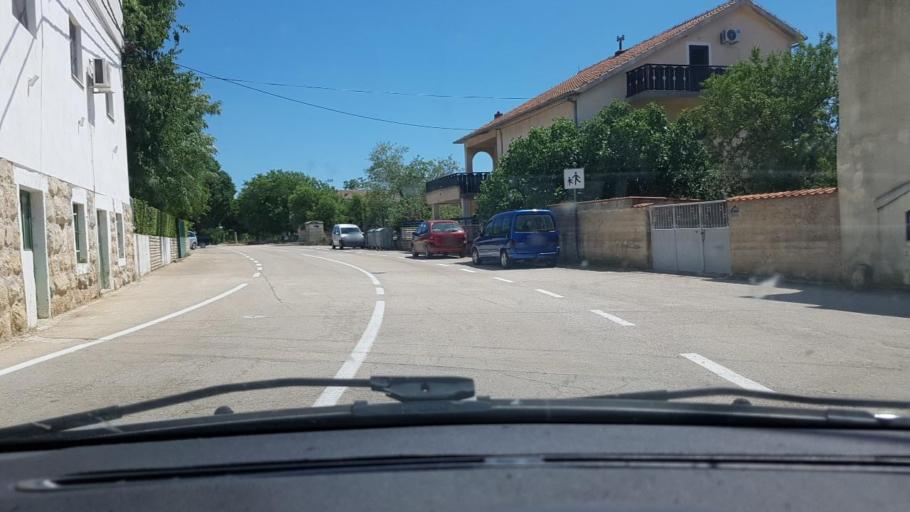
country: HR
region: Sibensko-Kniniska
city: Kistanje
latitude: 43.8883
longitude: 15.9102
